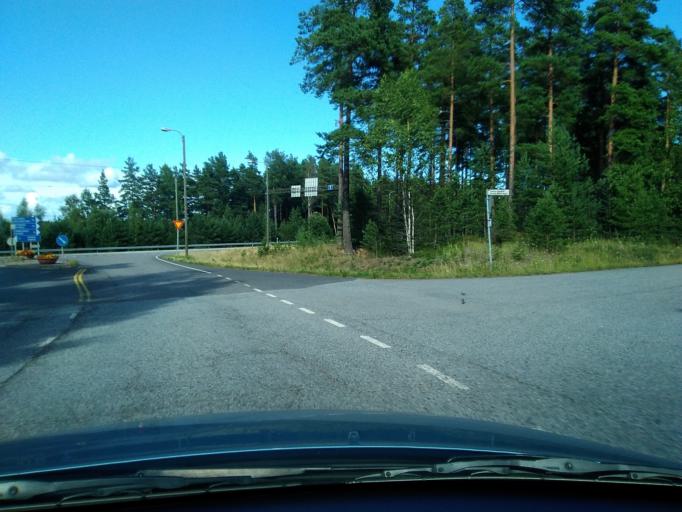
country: FI
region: Uusimaa
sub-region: Raaseporin
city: Ekenaes
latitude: 59.9055
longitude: 23.2373
